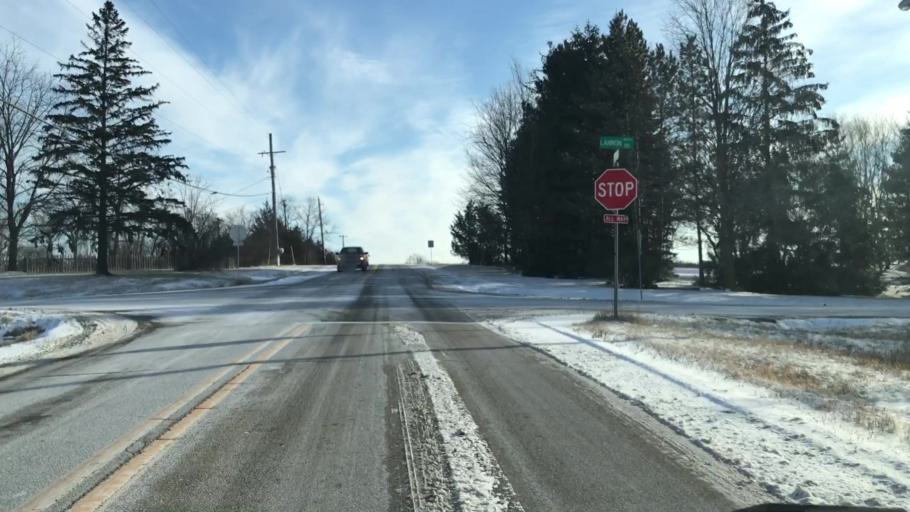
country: US
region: Wisconsin
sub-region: Waukesha County
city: Lannon
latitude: 43.1701
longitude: -88.1633
